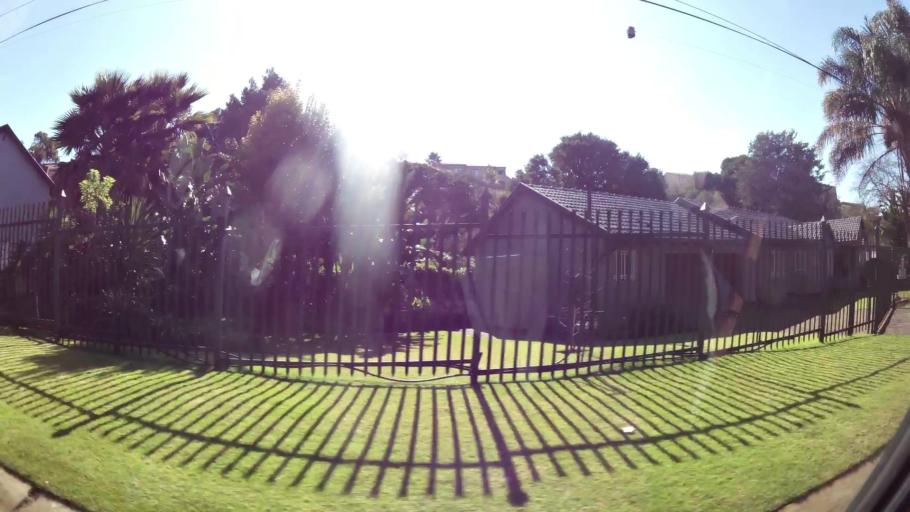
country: ZA
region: Gauteng
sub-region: City of Johannesburg Metropolitan Municipality
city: Roodepoort
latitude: -26.1179
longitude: 27.8559
